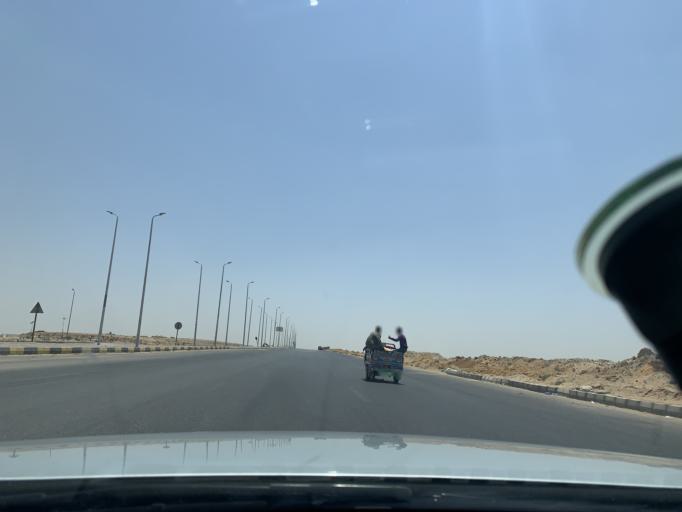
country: EG
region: Muhafazat al Qahirah
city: Halwan
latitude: 29.9920
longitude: 31.4687
